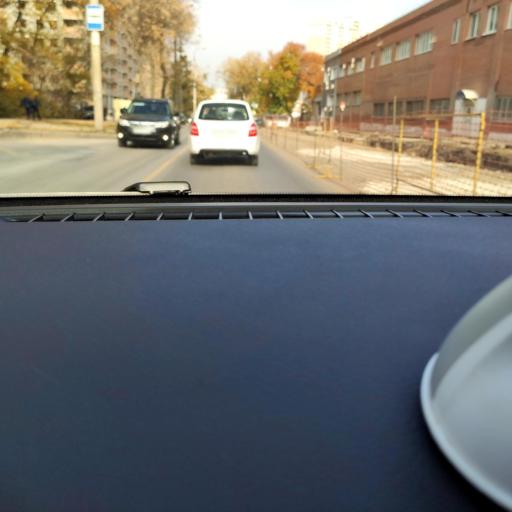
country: RU
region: Samara
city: Samara
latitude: 53.2039
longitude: 50.1782
